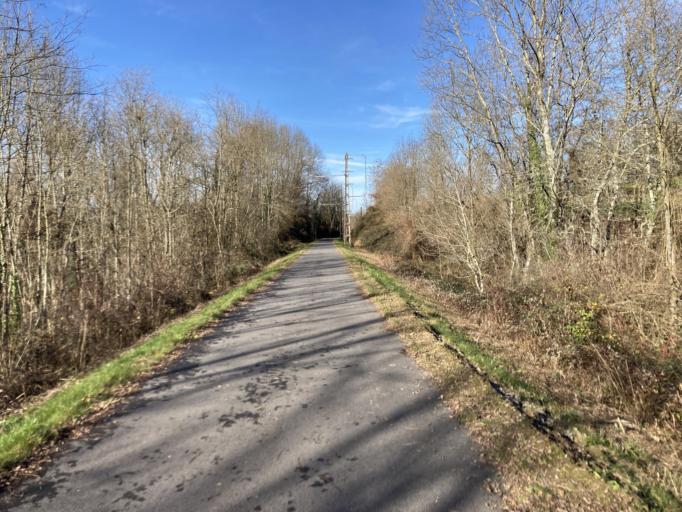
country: FR
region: Aquitaine
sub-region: Departement des Pyrenees-Atlantiques
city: Arudy
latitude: 43.1341
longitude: -0.4457
